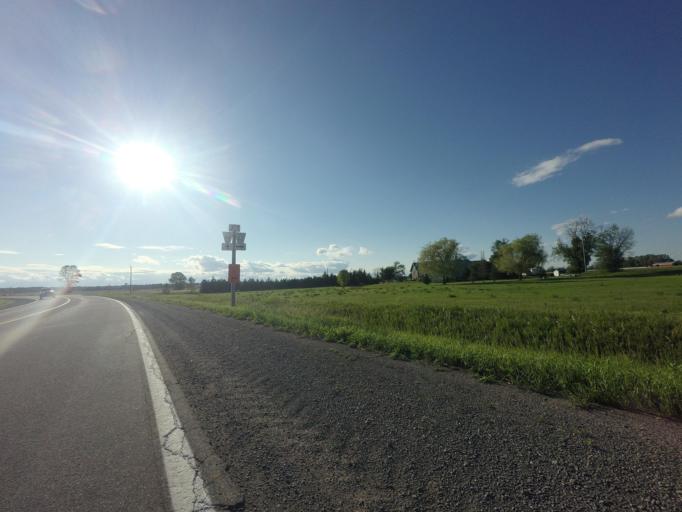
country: CA
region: Ontario
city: Arnprior
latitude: 45.3659
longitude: -76.3434
